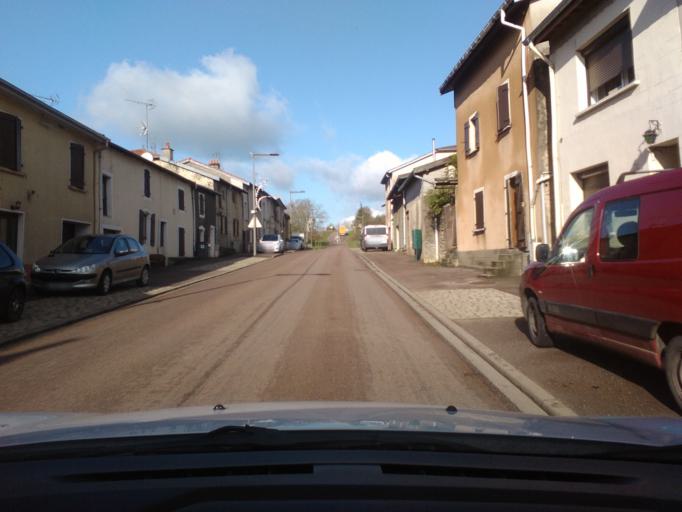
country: FR
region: Lorraine
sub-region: Departement des Vosges
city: Mirecourt
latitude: 48.3235
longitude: 6.1270
